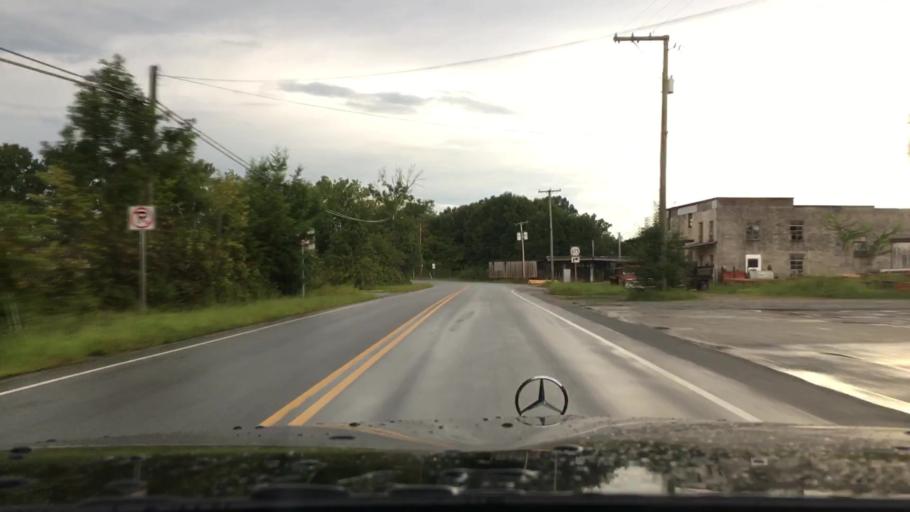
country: US
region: Virginia
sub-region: Amherst County
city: Amherst
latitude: 37.7145
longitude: -79.0221
